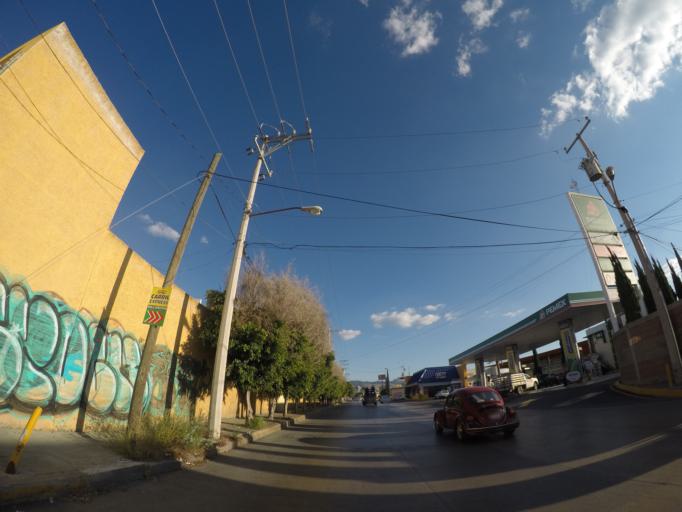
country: MX
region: San Luis Potosi
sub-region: San Luis Potosi
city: San Luis Potosi
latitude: 22.1573
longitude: -101.0018
